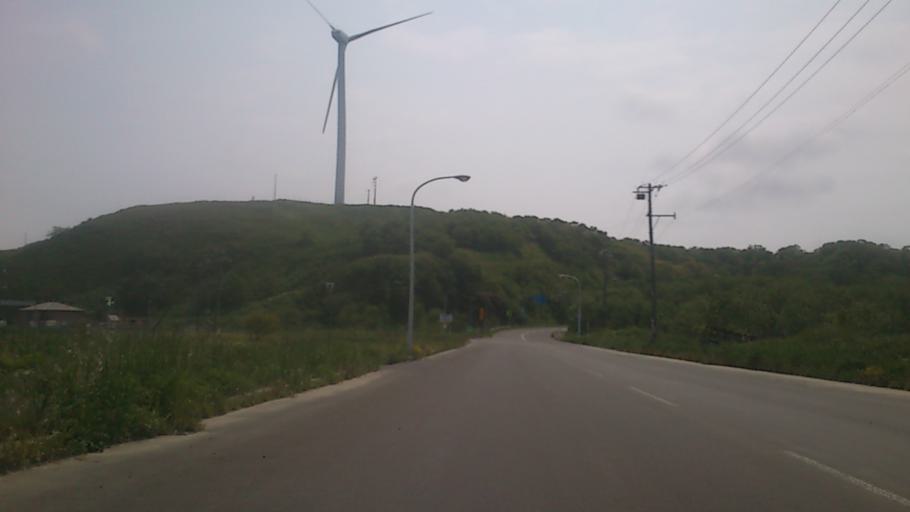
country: JP
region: Hokkaido
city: Nemuro
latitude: 43.2797
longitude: 145.5628
